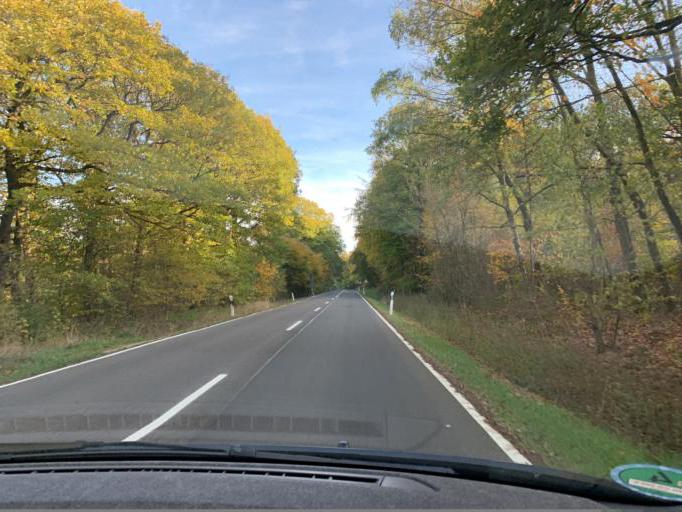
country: DE
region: North Rhine-Westphalia
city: Heimbach
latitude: 50.5920
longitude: 6.4980
